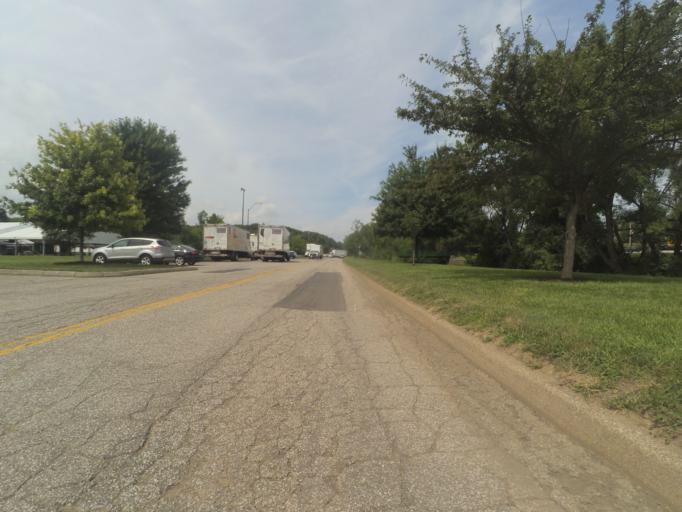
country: US
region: Ohio
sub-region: Cuyahoga County
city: Brooklyn
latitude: 41.4503
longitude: -81.7204
